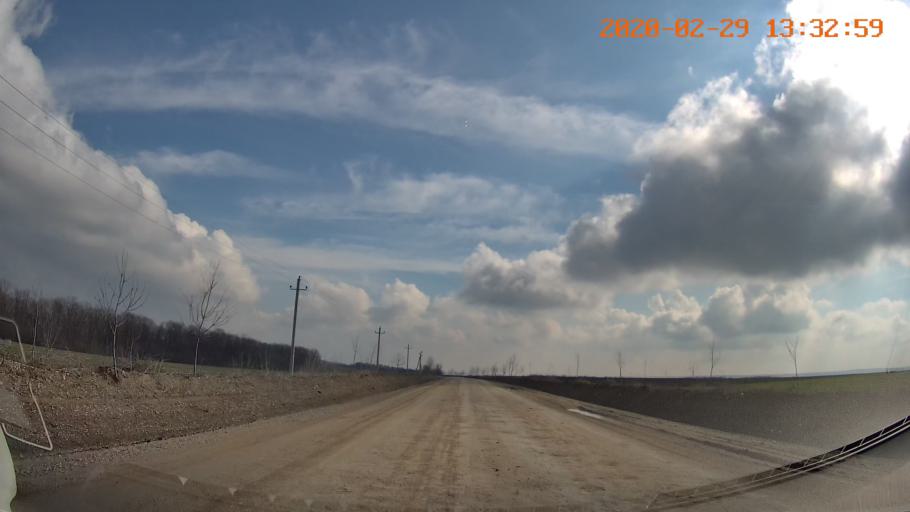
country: MD
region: Telenesti
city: Camenca
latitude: 47.8761
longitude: 28.6133
